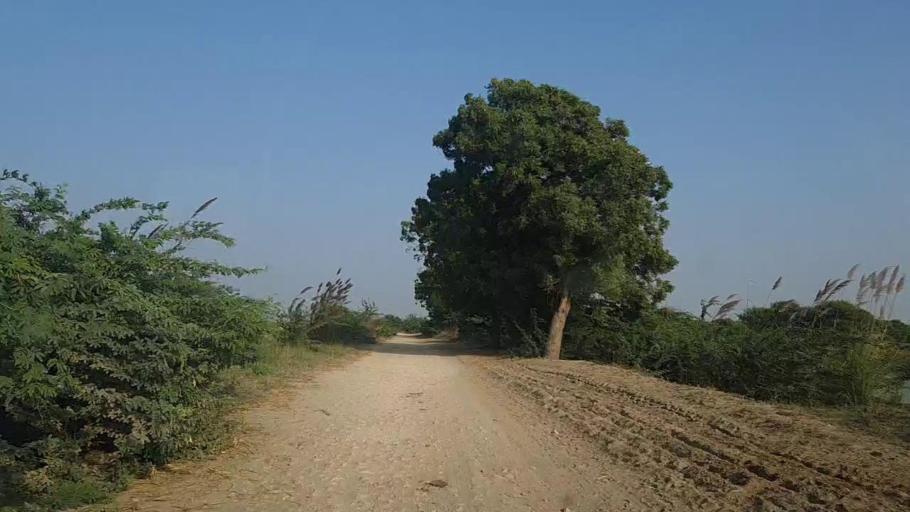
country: PK
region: Sindh
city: Mirpur Sakro
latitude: 24.5748
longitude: 67.6693
